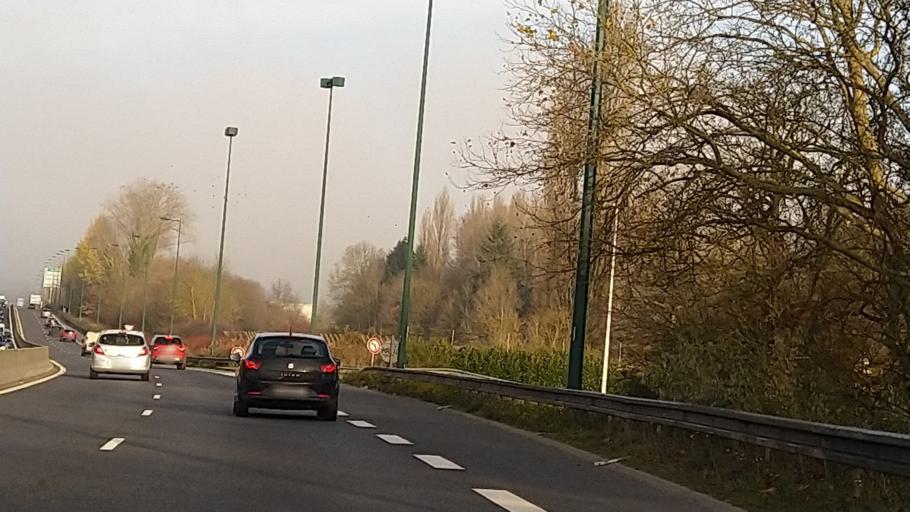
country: FR
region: Ile-de-France
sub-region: Departement du Val-d'Oise
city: Mours
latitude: 49.1341
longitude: 2.2563
